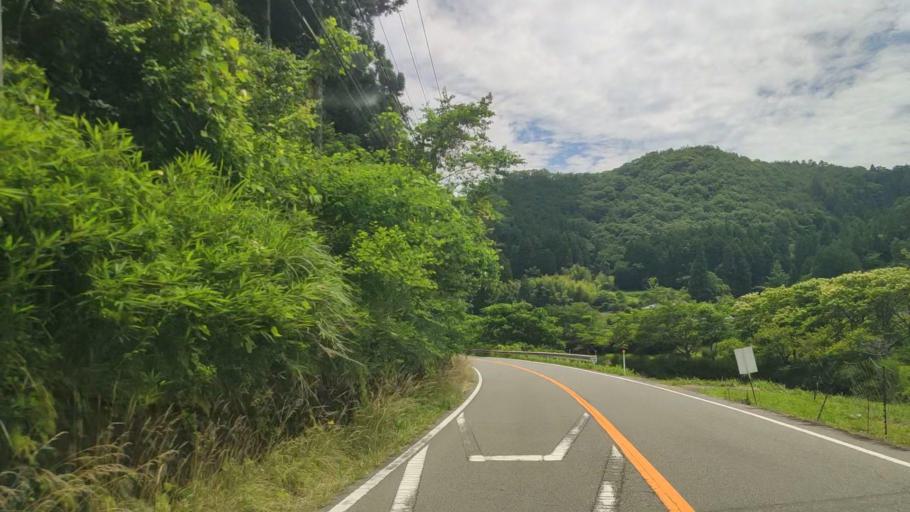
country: JP
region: Hyogo
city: Yamazakicho-nakabirose
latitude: 35.0833
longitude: 134.3581
